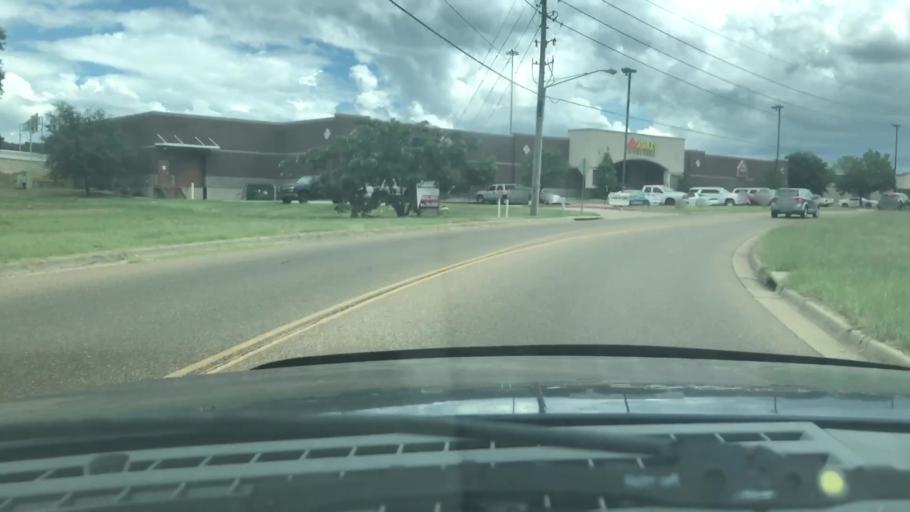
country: US
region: Texas
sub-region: Bowie County
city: Wake Village
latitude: 33.4494
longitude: -94.0989
